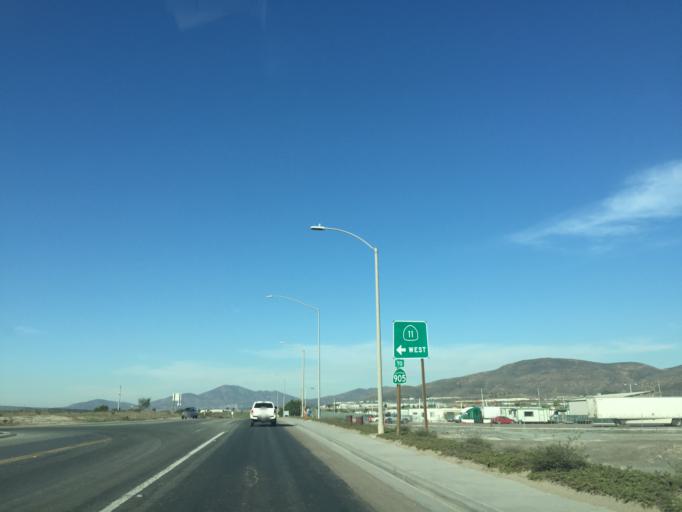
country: MX
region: Baja California
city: Tijuana
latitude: 32.5639
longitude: -116.9278
